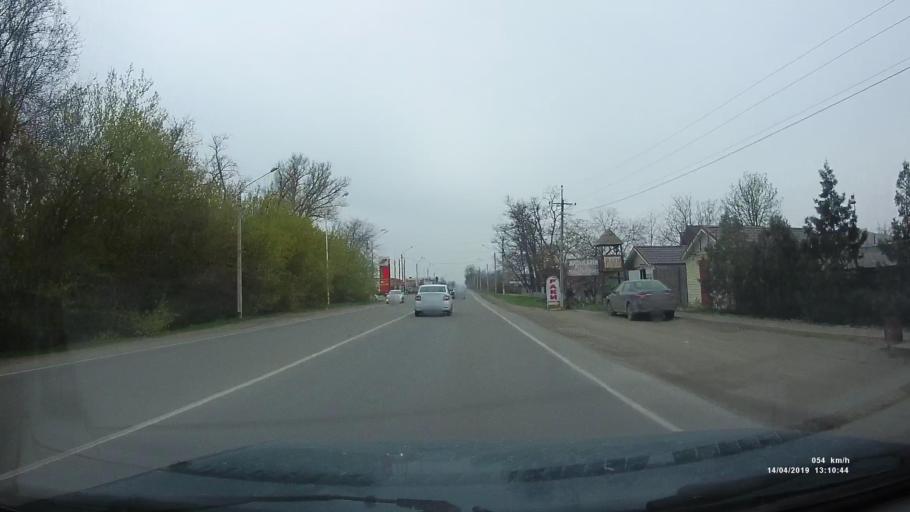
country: RU
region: Rostov
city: Kuleshovka
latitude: 47.1087
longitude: 39.6499
